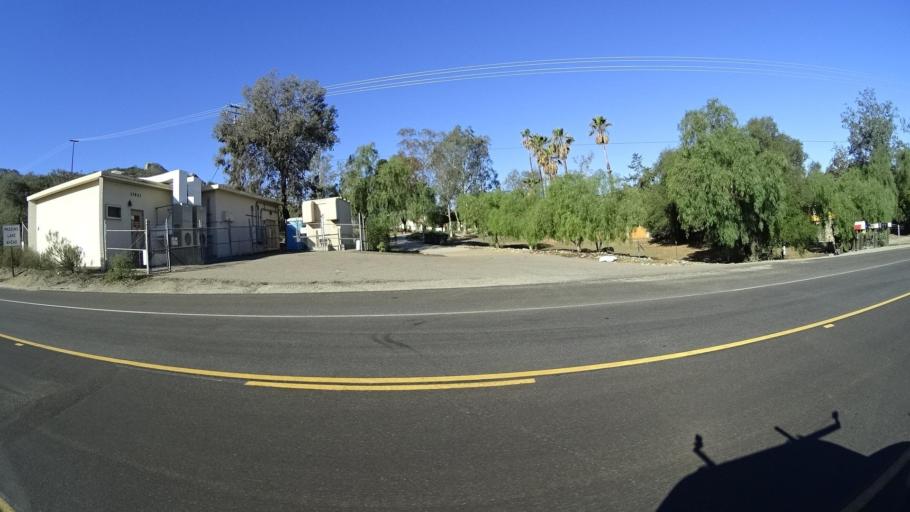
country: MX
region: Baja California
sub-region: Tijuana
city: Villa del Campo
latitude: 32.6278
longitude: -116.7649
